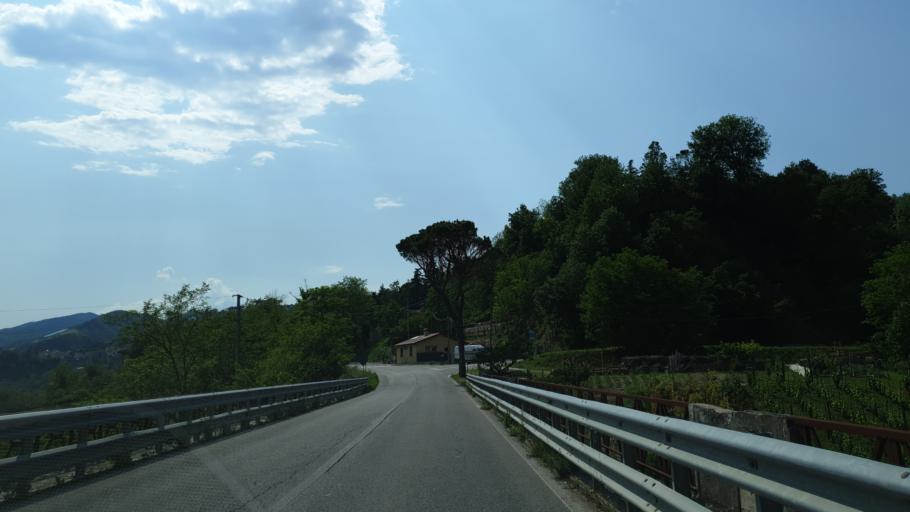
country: IT
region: Emilia-Romagna
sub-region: Forli-Cesena
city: Sarsina
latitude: 43.9241
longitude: 12.1627
